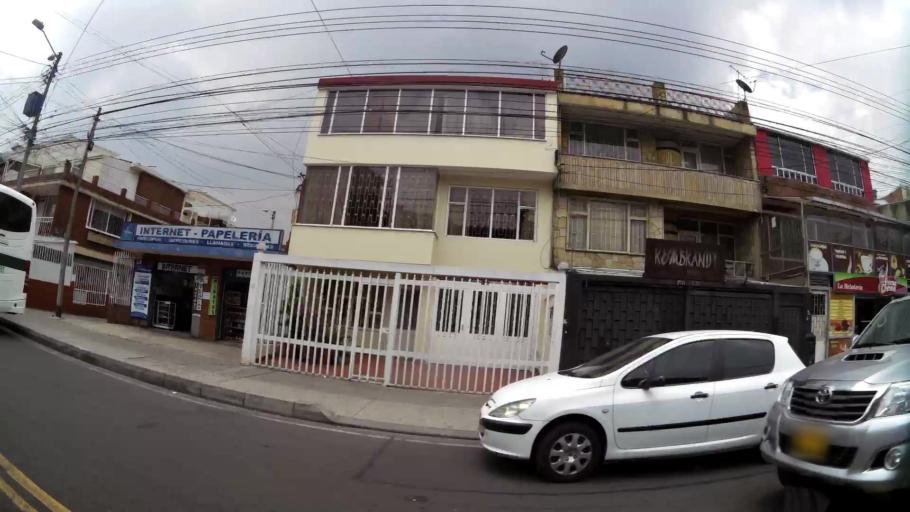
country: CO
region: Bogota D.C.
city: Bogota
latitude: 4.6151
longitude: -74.1092
